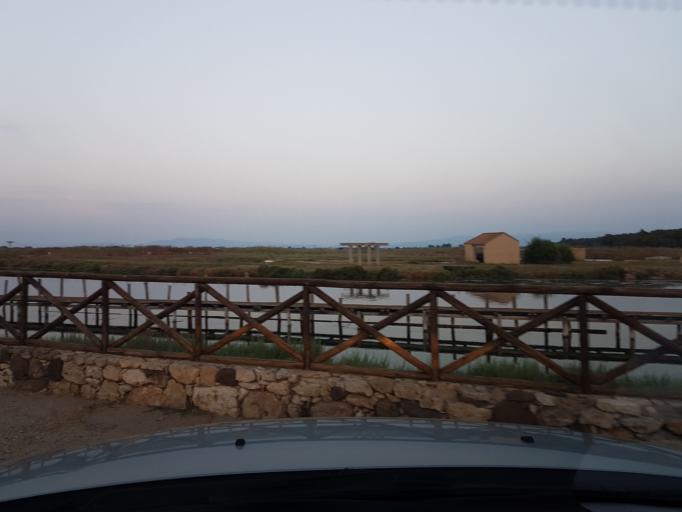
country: IT
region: Sardinia
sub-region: Provincia di Oristano
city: Cabras
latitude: 39.9138
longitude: 8.5090
